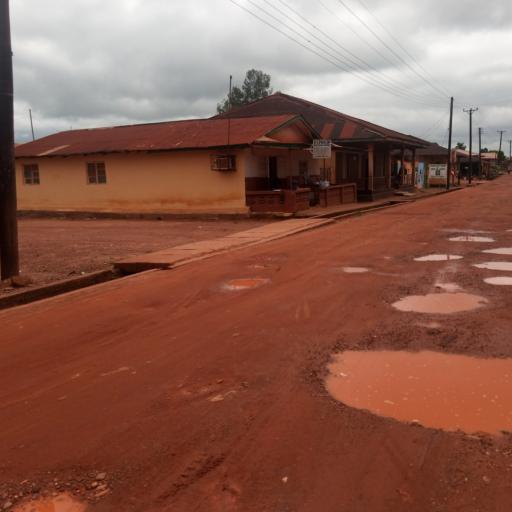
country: SL
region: Eastern Province
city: Kenema
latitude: 7.8851
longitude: -11.1876
